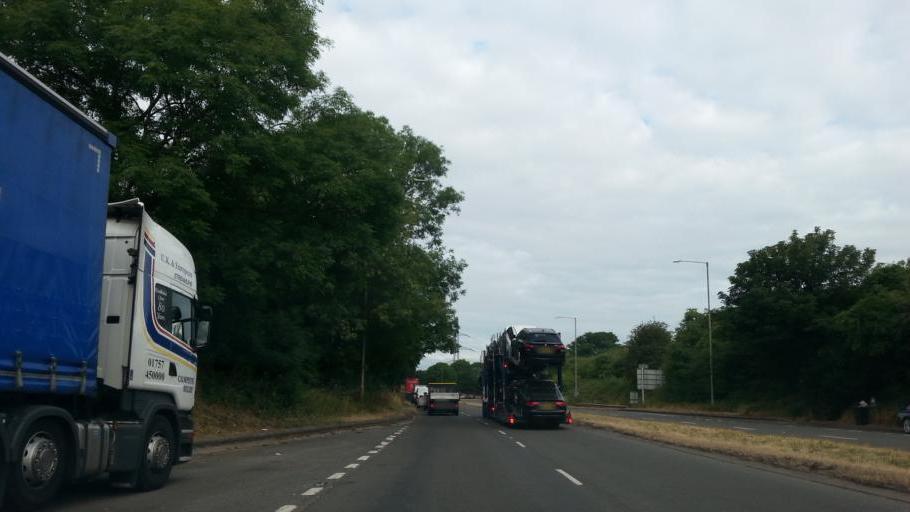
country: GB
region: England
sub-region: Warwickshire
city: Exhall
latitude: 52.4592
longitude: -1.4885
